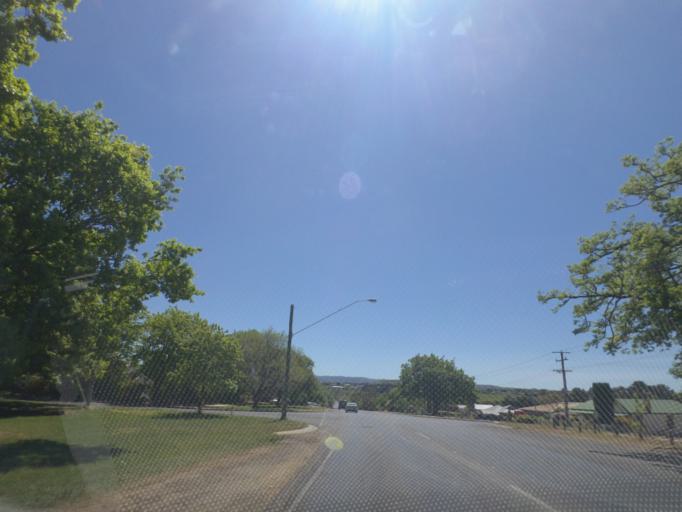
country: AU
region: Victoria
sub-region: Hume
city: Sunbury
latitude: -37.4924
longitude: 144.5903
